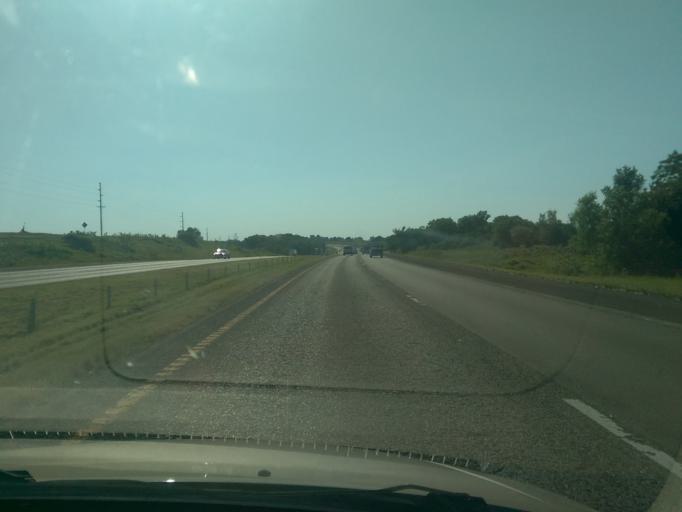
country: US
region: Missouri
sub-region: Lafayette County
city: Concordia
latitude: 38.9901
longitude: -93.6420
